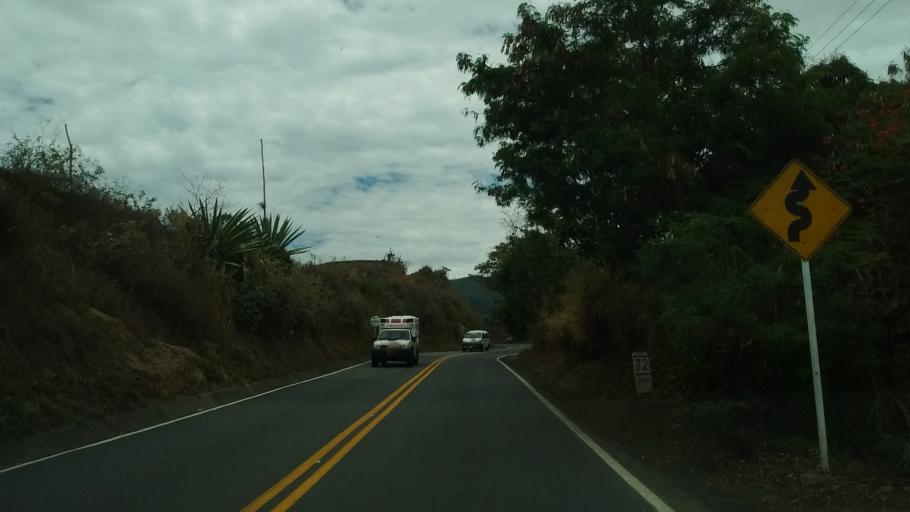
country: CO
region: Cauca
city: La Sierra
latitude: 2.2282
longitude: -76.7953
